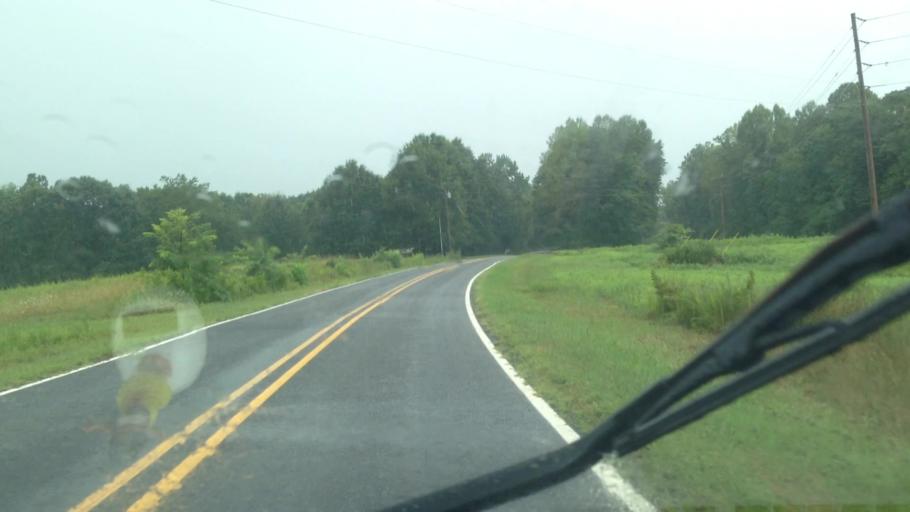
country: US
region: North Carolina
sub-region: Stokes County
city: Danbury
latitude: 36.4368
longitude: -80.0886
